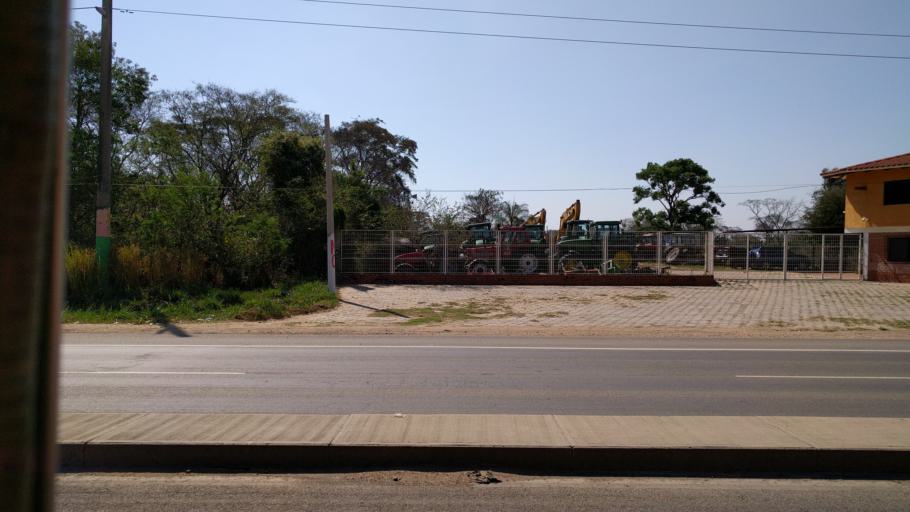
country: BO
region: Santa Cruz
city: Cotoca
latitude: -17.7673
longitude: -63.0523
